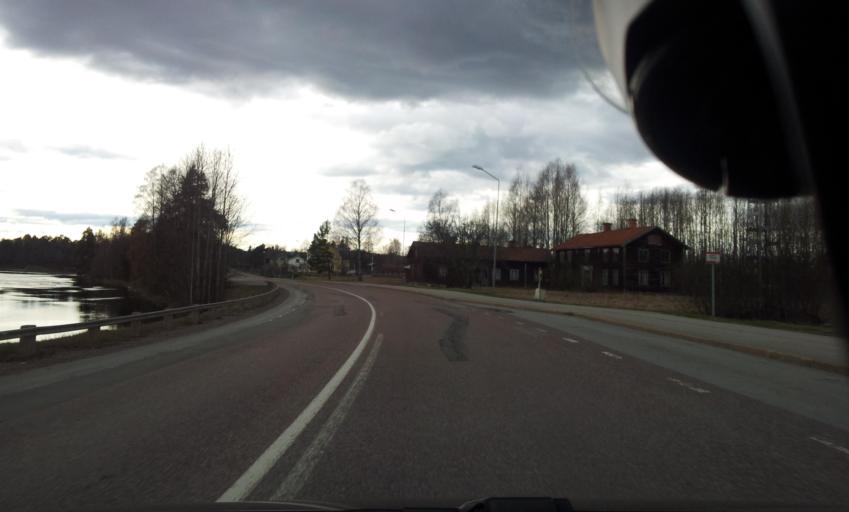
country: SE
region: Gaevleborg
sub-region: Ljusdals Kommun
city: Ljusdal
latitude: 61.8367
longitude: 16.0624
